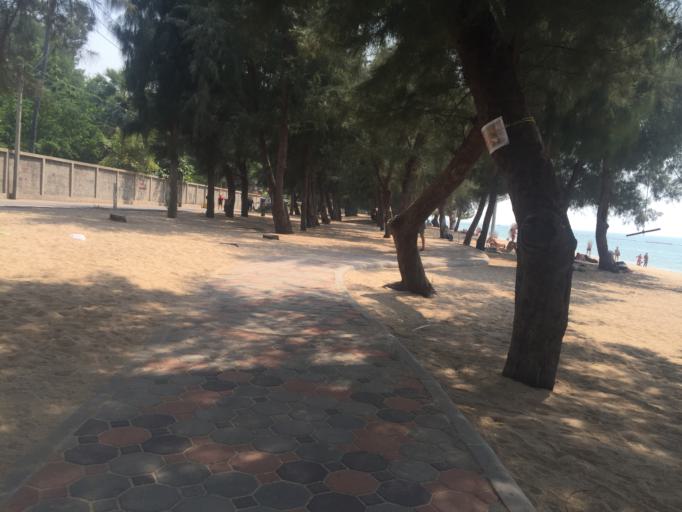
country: TH
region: Chon Buri
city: Phatthaya
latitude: 12.9032
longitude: 100.8622
